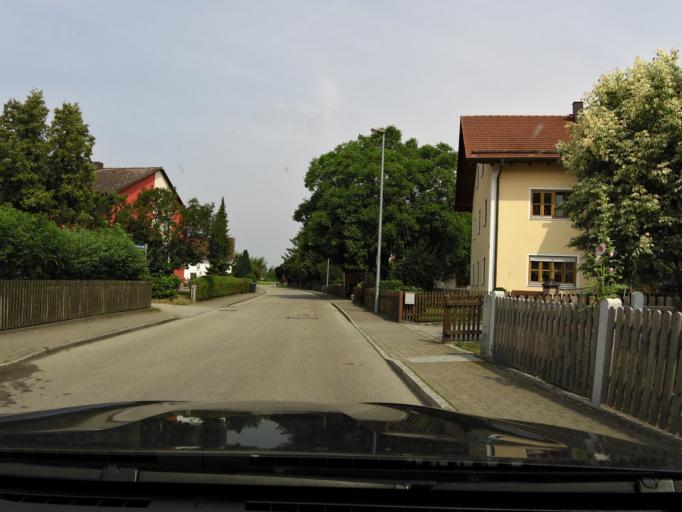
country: DE
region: Bavaria
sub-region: Upper Bavaria
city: Eitting
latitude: 48.3631
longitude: 11.8903
